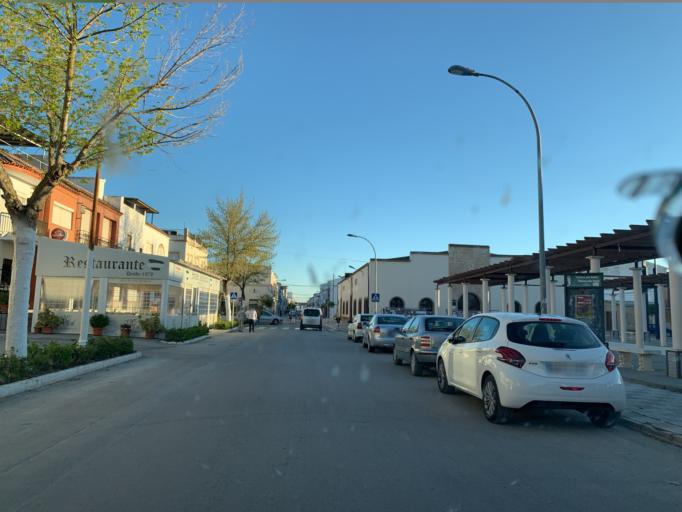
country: ES
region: Andalusia
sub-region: Provincia de Sevilla
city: Pedrera
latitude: 37.2273
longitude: -4.8933
